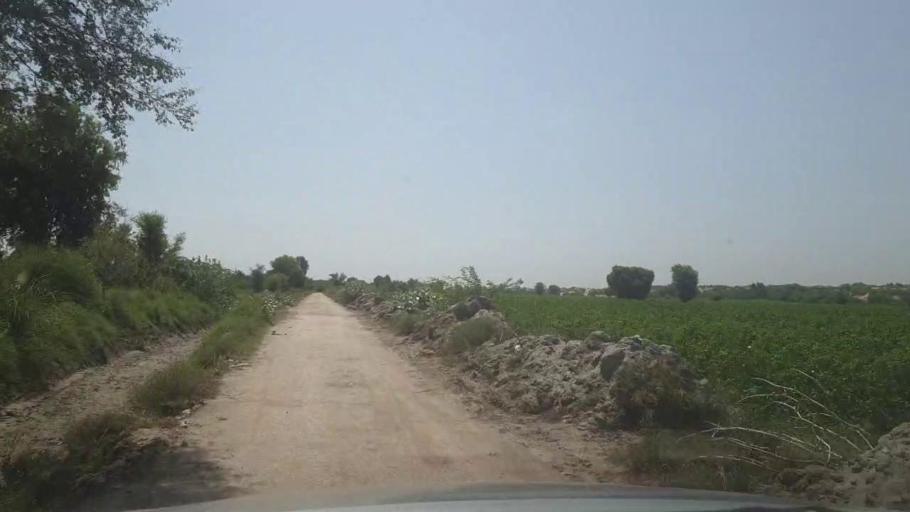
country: PK
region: Sindh
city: Khairpur
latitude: 27.3583
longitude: 69.0370
